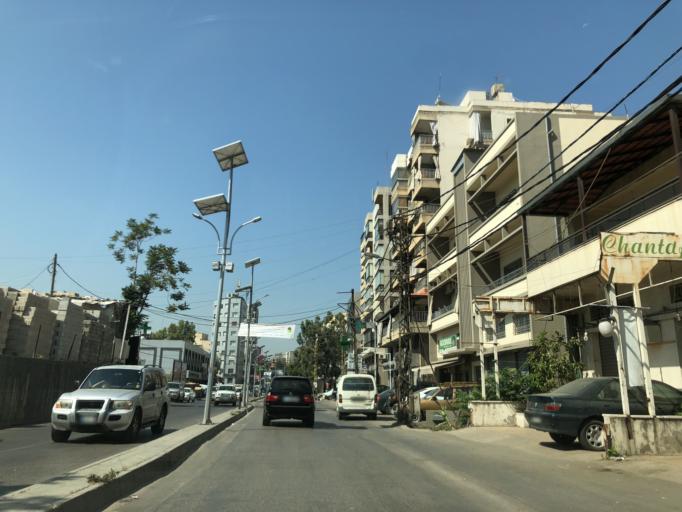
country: LB
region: Mont-Liban
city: Jdaidet el Matn
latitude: 33.8741
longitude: 35.5466
